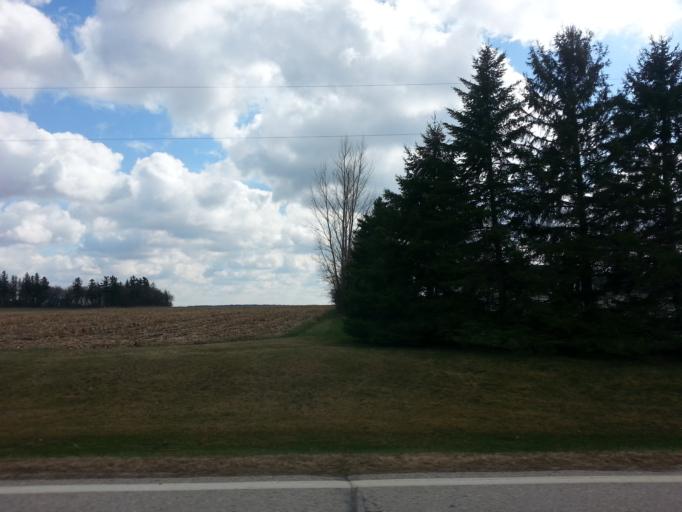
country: US
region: Minnesota
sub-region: Olmsted County
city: Byron
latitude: 44.0940
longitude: -92.6814
